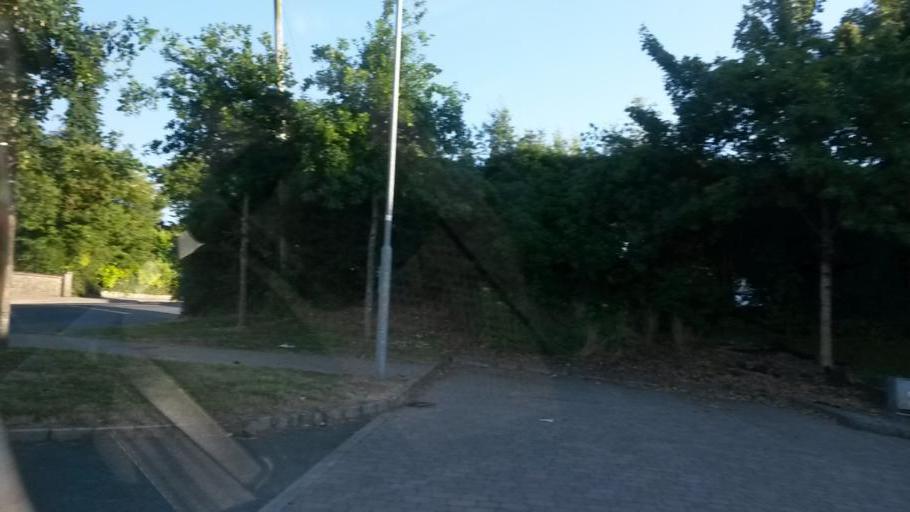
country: IE
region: Leinster
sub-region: An Mhi
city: Ashbourne
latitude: 53.5636
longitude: -6.3847
